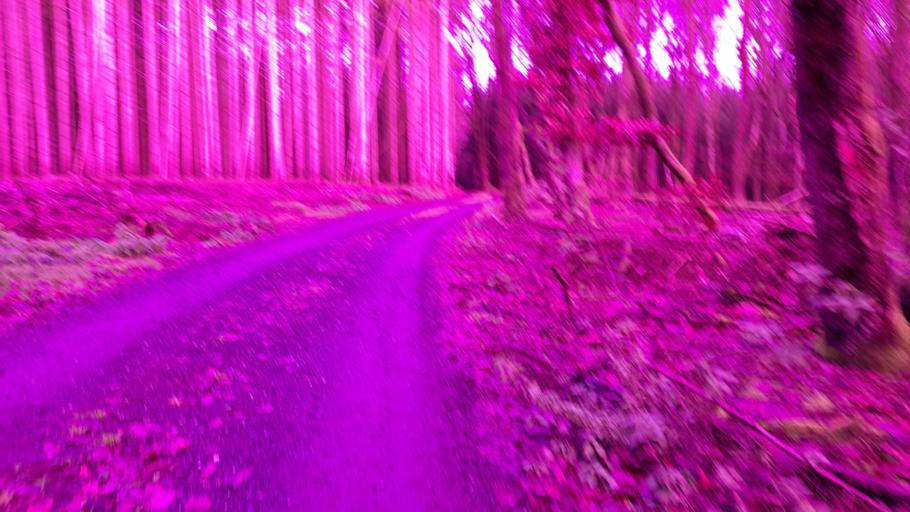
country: DE
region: Rheinland-Pfalz
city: Dasburg
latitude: 50.0735
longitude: 6.1100
